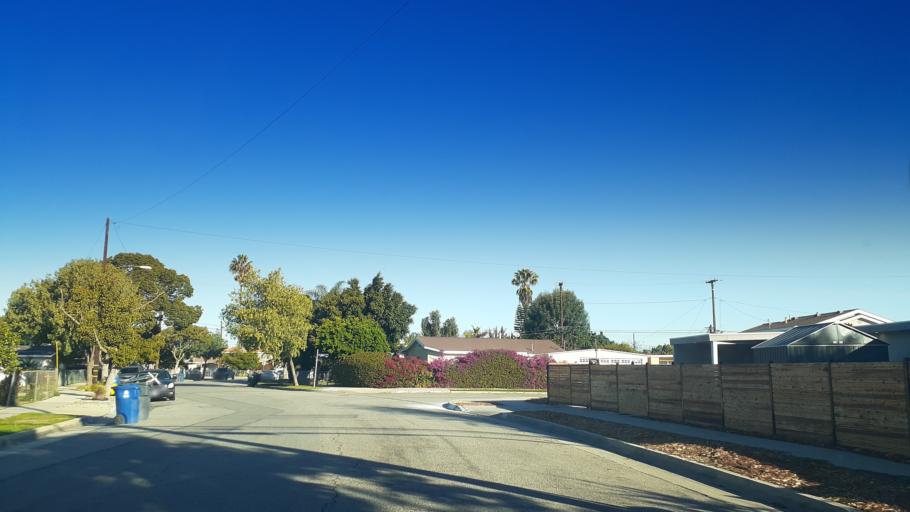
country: US
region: California
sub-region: Los Angeles County
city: Hawaiian Gardens
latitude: 33.8431
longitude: -118.0807
